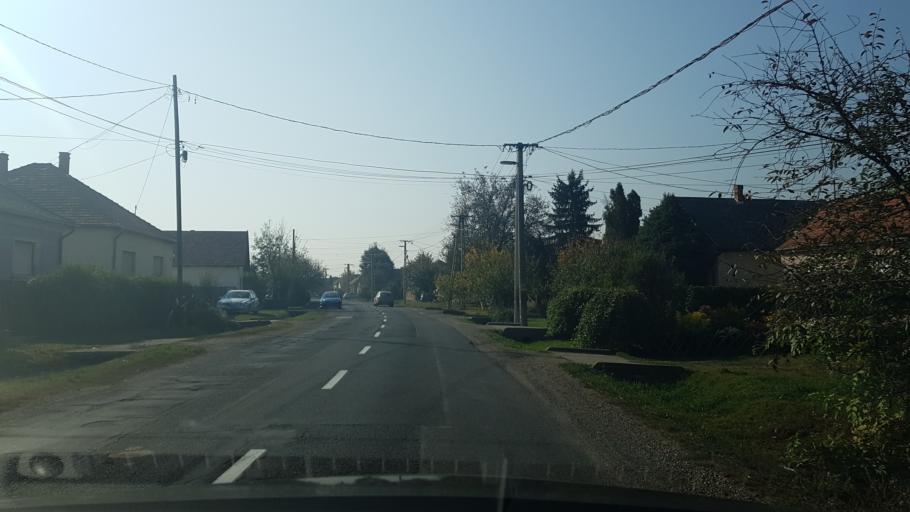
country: HU
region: Fejer
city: Adony
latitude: 47.1155
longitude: 18.8608
